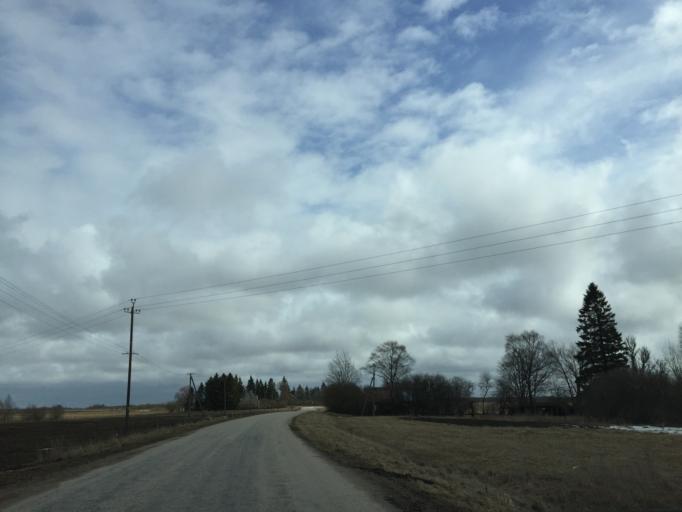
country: EE
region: Laeaene
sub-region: Lihula vald
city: Lihula
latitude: 58.7329
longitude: 23.8673
